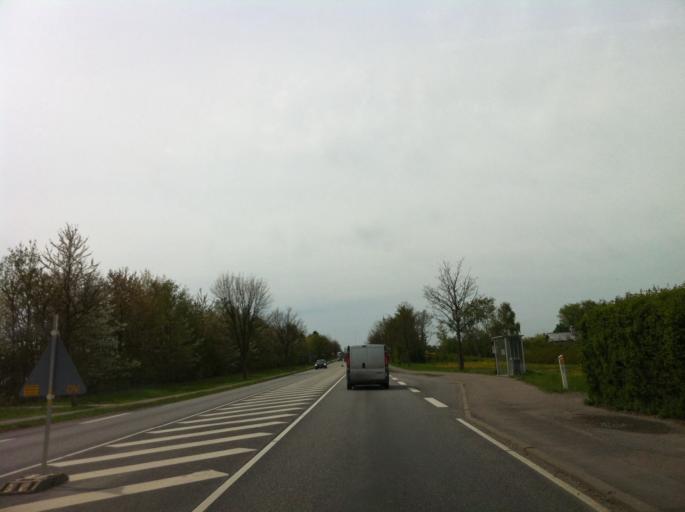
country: DK
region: Zealand
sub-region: Roskilde Kommune
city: Svogerslev
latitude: 55.5959
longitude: 12.0161
